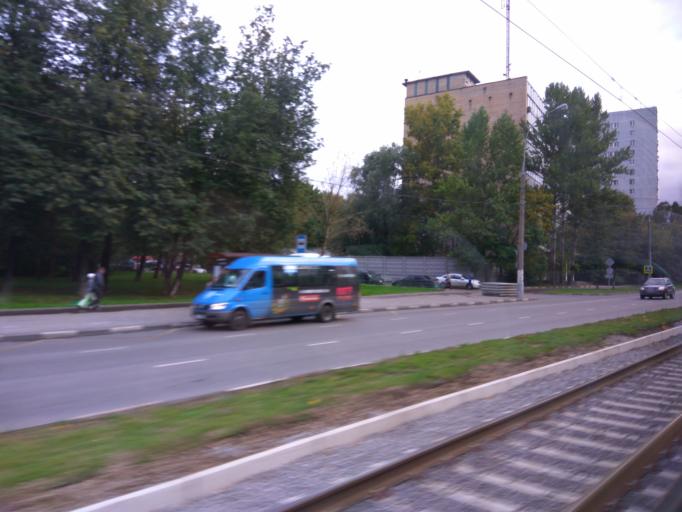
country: RU
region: Moscow
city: Nagornyy
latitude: 55.6318
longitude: 37.6015
